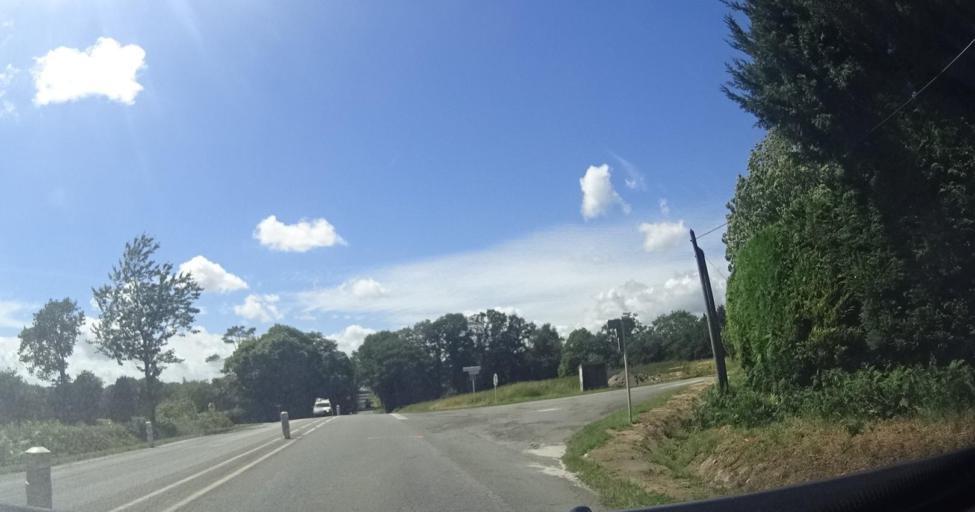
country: FR
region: Brittany
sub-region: Departement du Morbihan
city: Questembert
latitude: 47.6908
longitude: -2.4781
